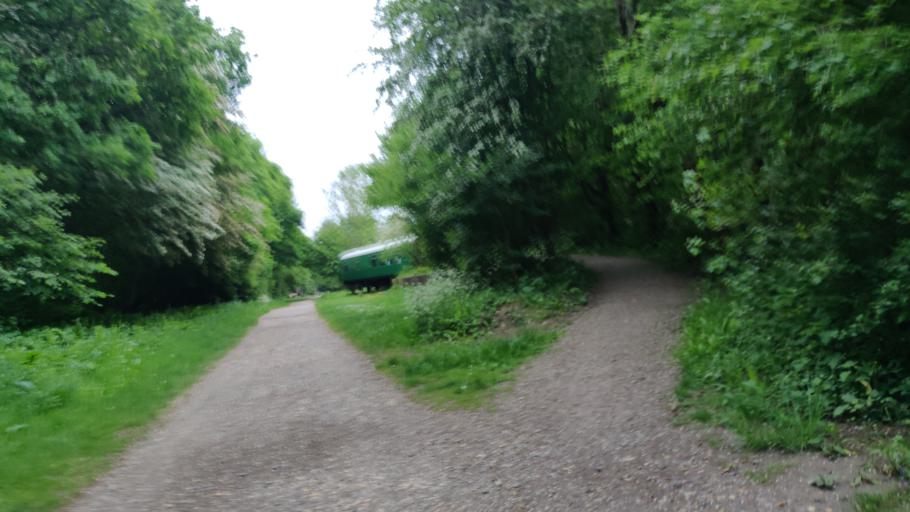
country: GB
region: England
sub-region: West Sussex
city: Partridge Green
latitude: 50.9918
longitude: -0.3146
